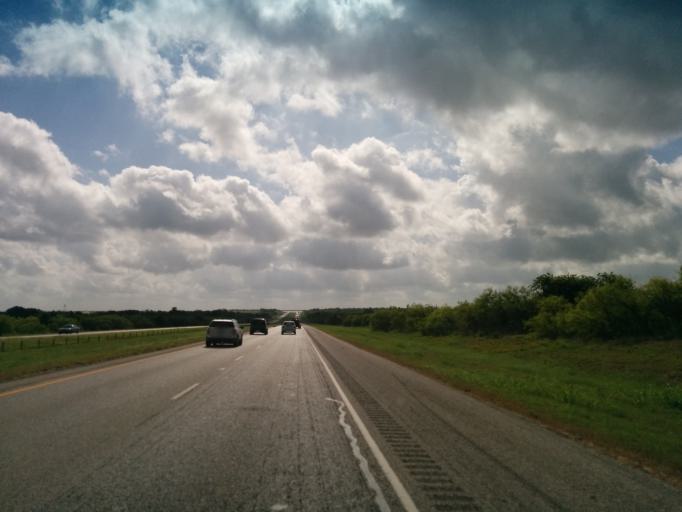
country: US
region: Texas
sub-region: Gonzales County
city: Waelder
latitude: 29.6649
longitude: -97.3533
